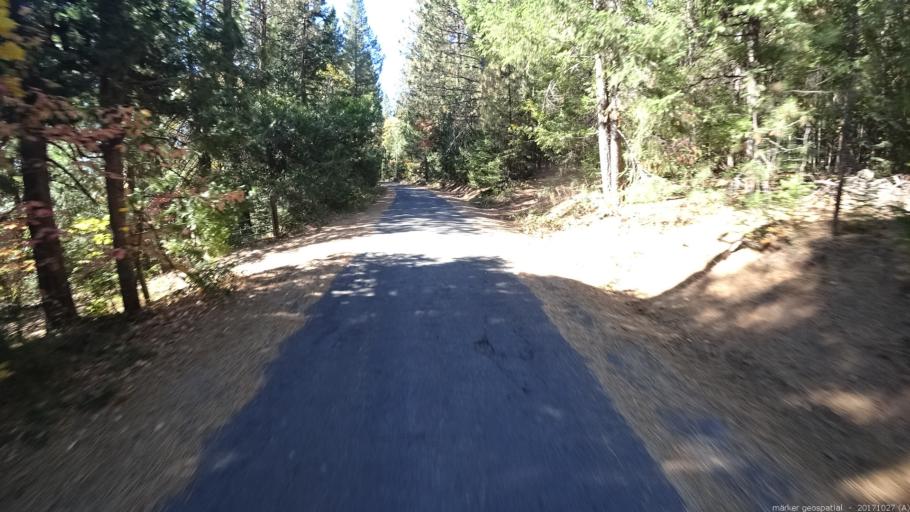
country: US
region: California
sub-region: Shasta County
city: Shingletown
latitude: 40.7211
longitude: -121.9305
